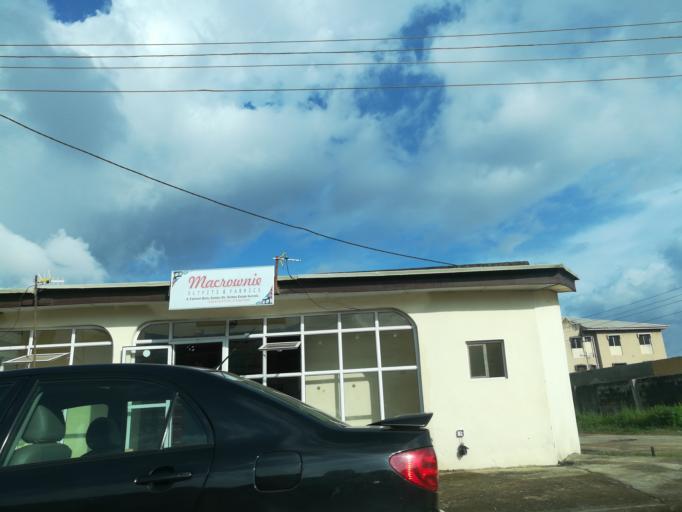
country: NG
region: Lagos
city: Ebute Ikorodu
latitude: 6.5990
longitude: 3.5008
